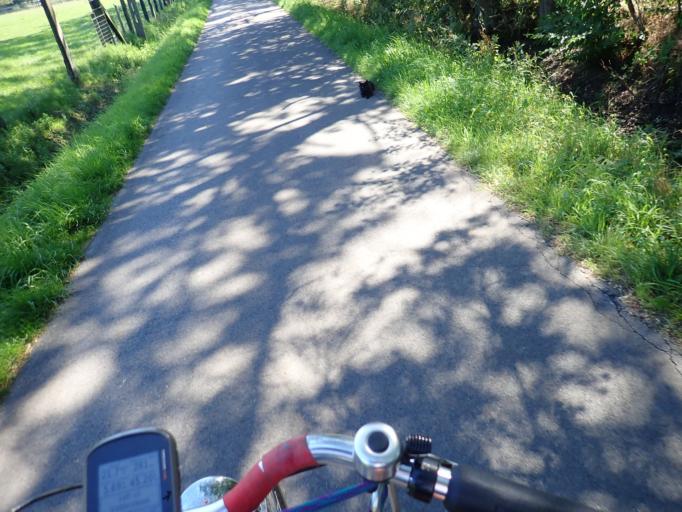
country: BE
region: Flanders
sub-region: Provincie Antwerpen
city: Herselt
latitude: 51.0503
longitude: 4.9111
